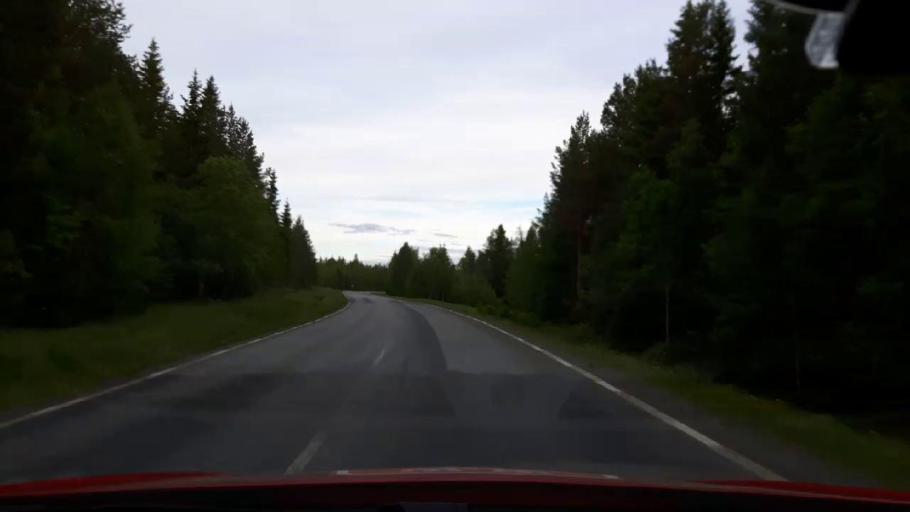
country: SE
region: Jaemtland
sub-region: OEstersunds Kommun
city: Ostersund
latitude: 63.0722
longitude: 14.4451
